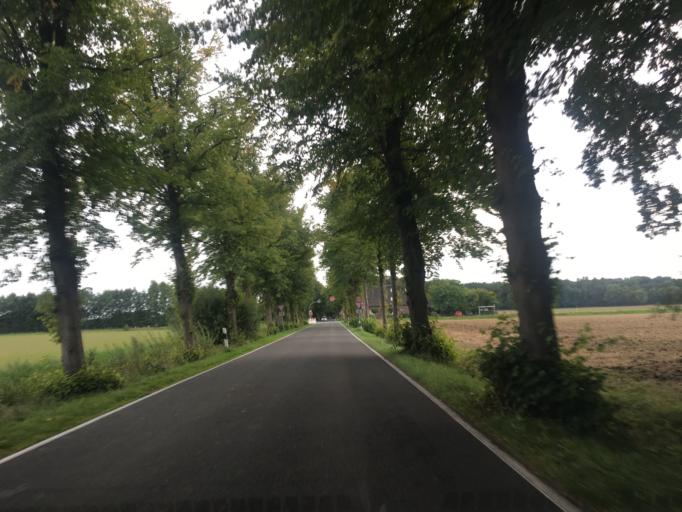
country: DE
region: North Rhine-Westphalia
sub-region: Regierungsbezirk Munster
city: Havixbeck
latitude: 51.9544
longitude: 7.5094
